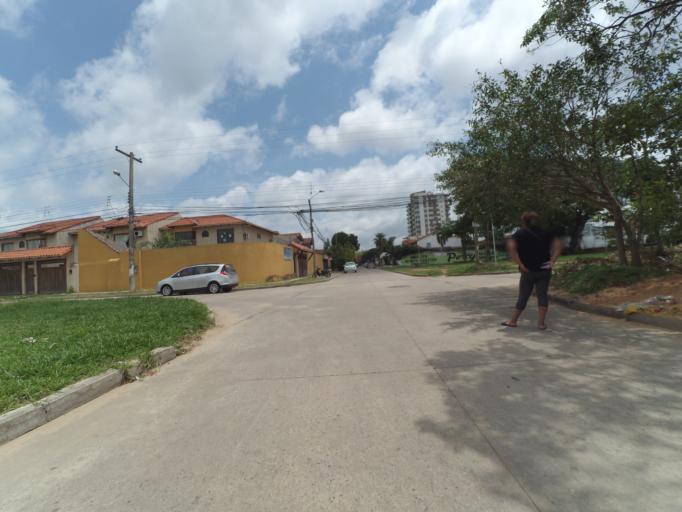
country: BO
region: Santa Cruz
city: Santa Cruz de la Sierra
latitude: -17.7879
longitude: -63.2128
